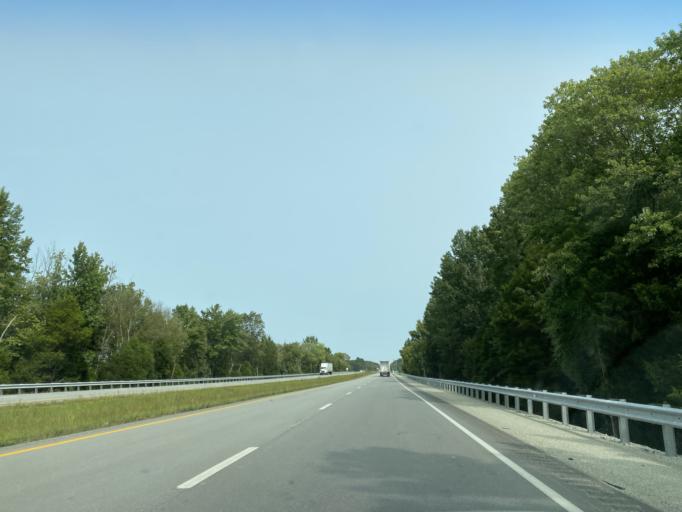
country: US
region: Kentucky
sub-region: Bullitt County
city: Lebanon Junction
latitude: 37.7477
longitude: -85.6800
